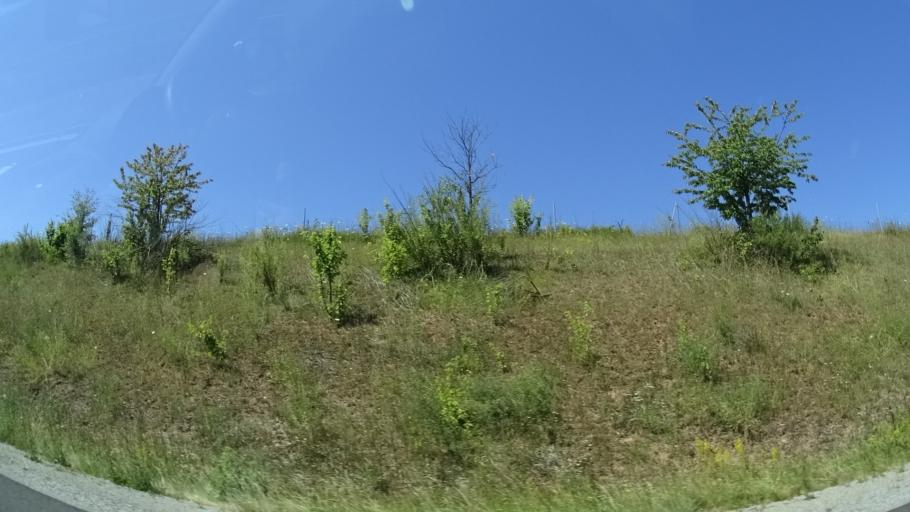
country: DE
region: Bavaria
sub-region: Regierungsbezirk Unterfranken
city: Geldersheim
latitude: 50.0436
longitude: 10.1390
